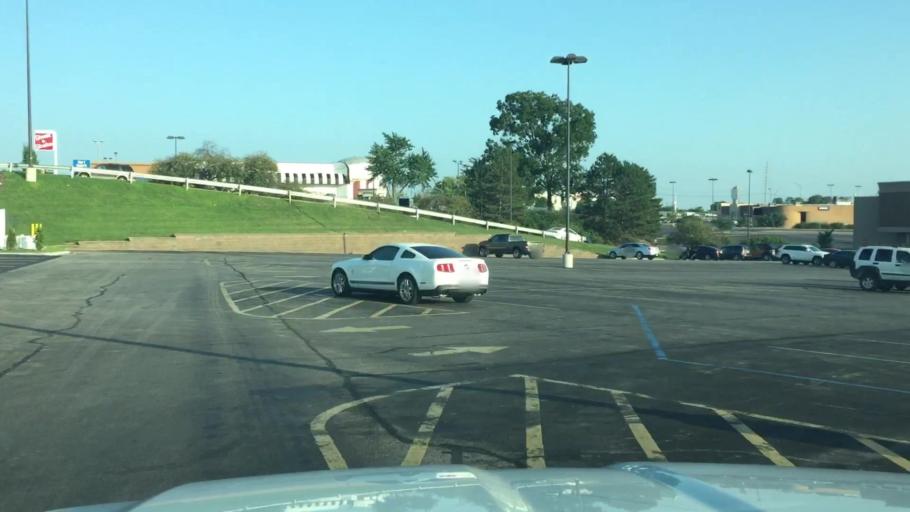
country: US
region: Missouri
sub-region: Saint Louis County
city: Mehlville
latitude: 38.5076
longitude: -90.3295
